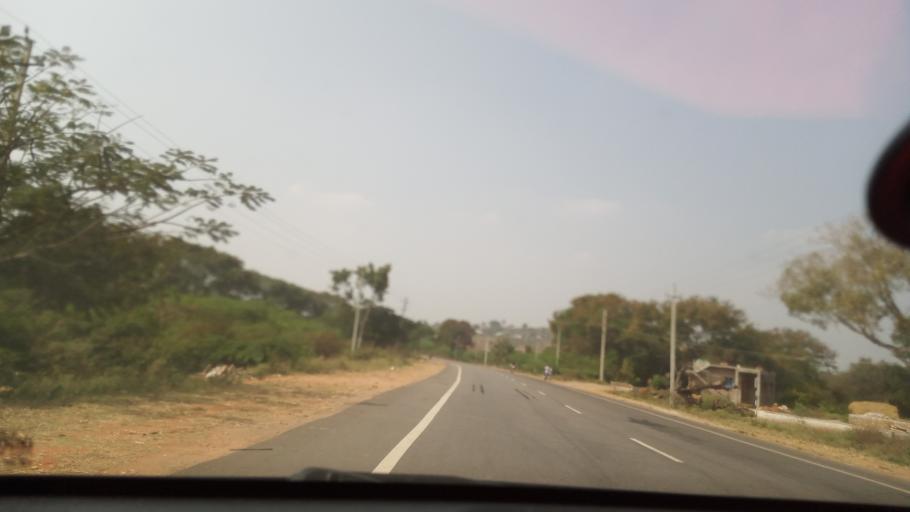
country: IN
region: Karnataka
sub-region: Mysore
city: Nanjangud
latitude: 12.0872
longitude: 76.7295
